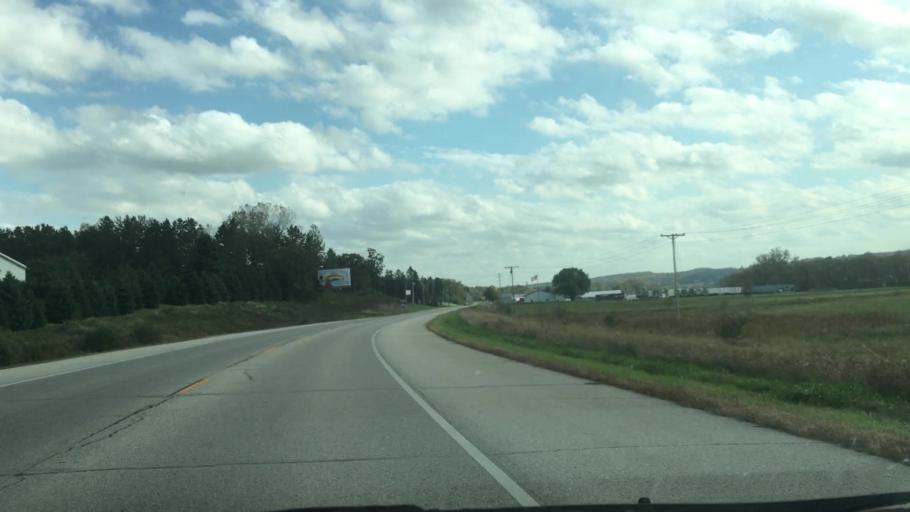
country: US
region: Minnesota
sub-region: Fillmore County
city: Chatfield
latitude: 43.8633
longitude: -92.1971
